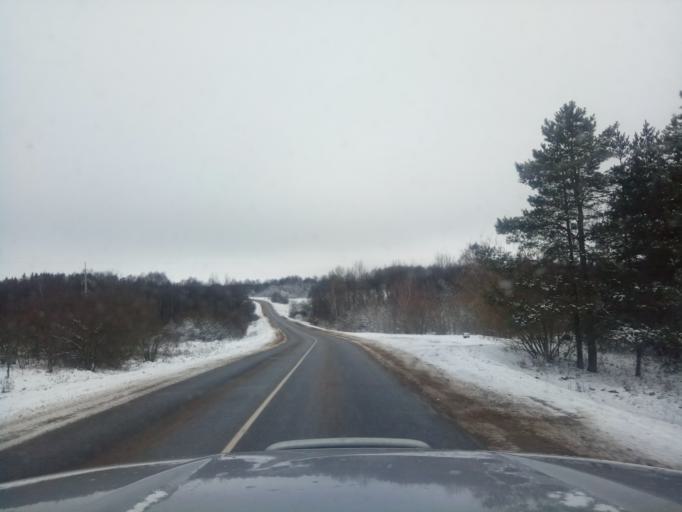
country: BY
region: Minsk
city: Kapyl'
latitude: 53.1509
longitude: 27.1221
